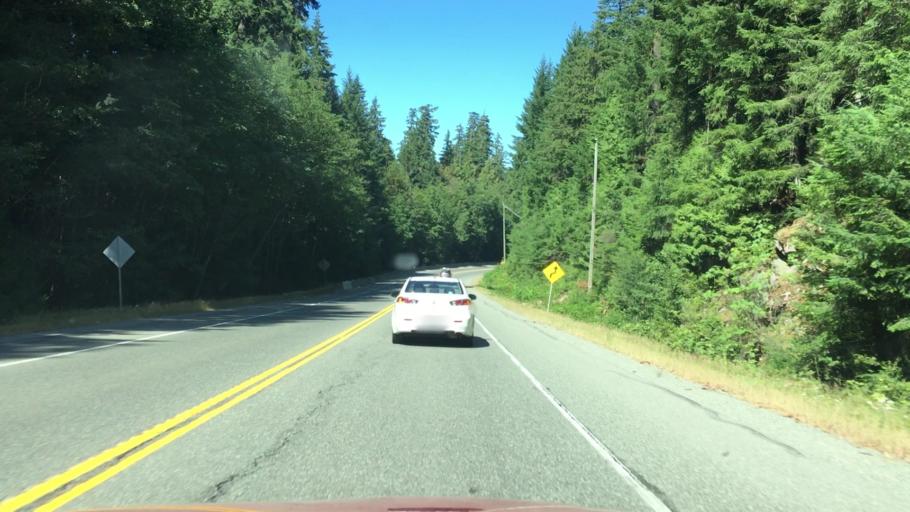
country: CA
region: British Columbia
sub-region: Regional District of Nanaimo
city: Parksville
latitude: 49.2984
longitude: -124.5590
